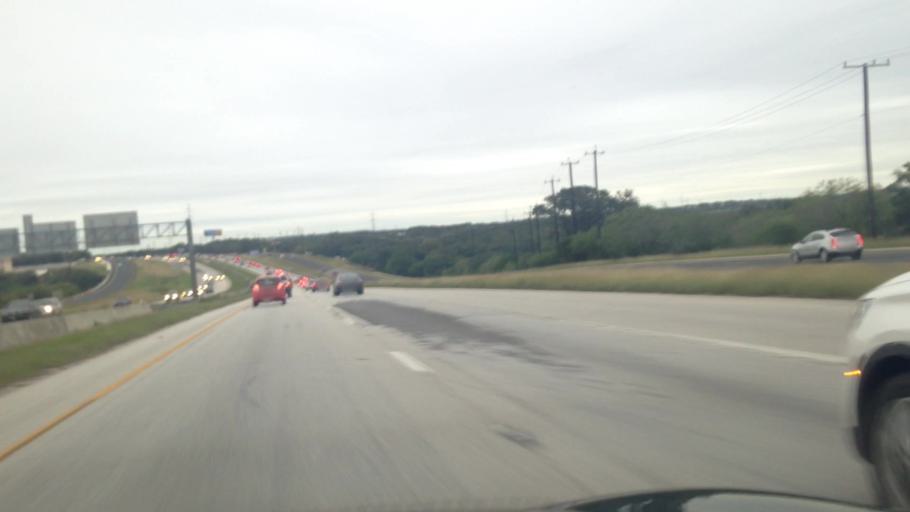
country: US
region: Texas
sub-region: Bexar County
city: Hollywood Park
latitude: 29.6010
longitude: -98.4369
